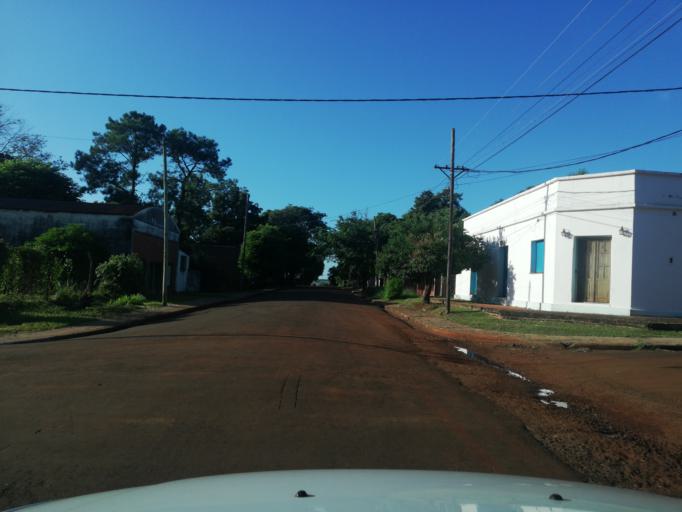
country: AR
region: Misiones
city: Garupa
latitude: -27.4840
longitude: -55.8279
